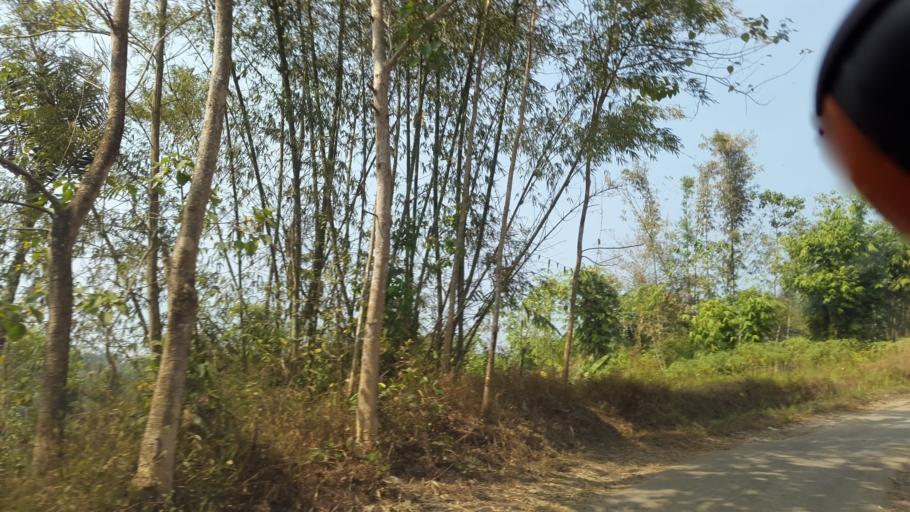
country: ID
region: West Java
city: Citampian
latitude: -7.1617
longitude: 106.7605
